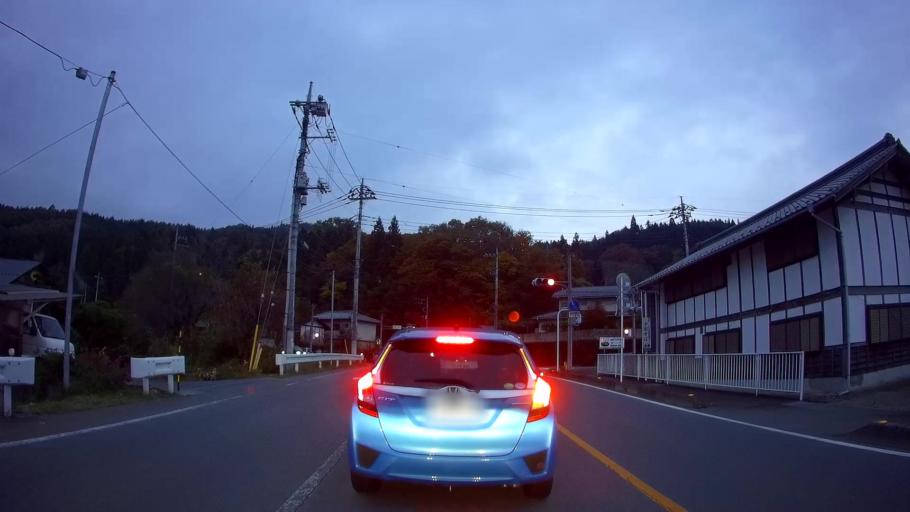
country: JP
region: Gunma
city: Nakanojomachi
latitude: 36.5455
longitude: 138.8028
